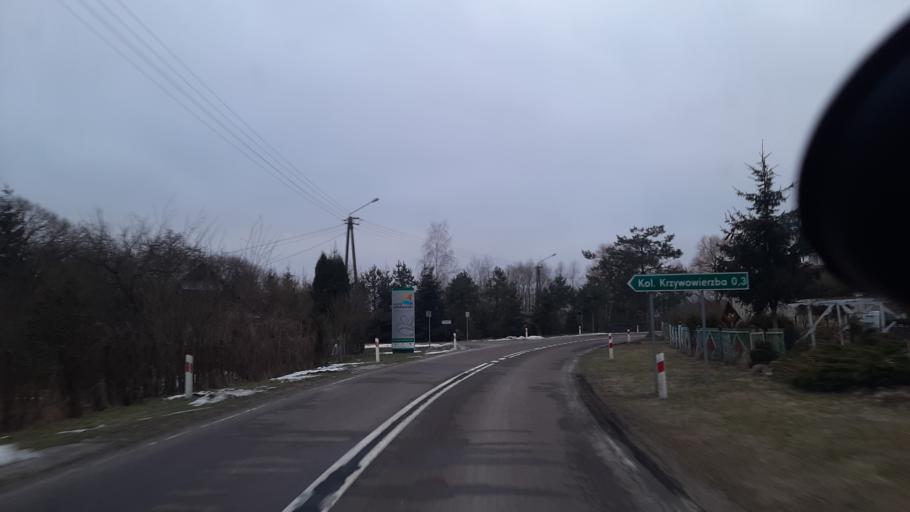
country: PL
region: Lublin Voivodeship
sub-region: Powiat parczewski
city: Podedworze
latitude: 51.5918
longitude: 23.1825
